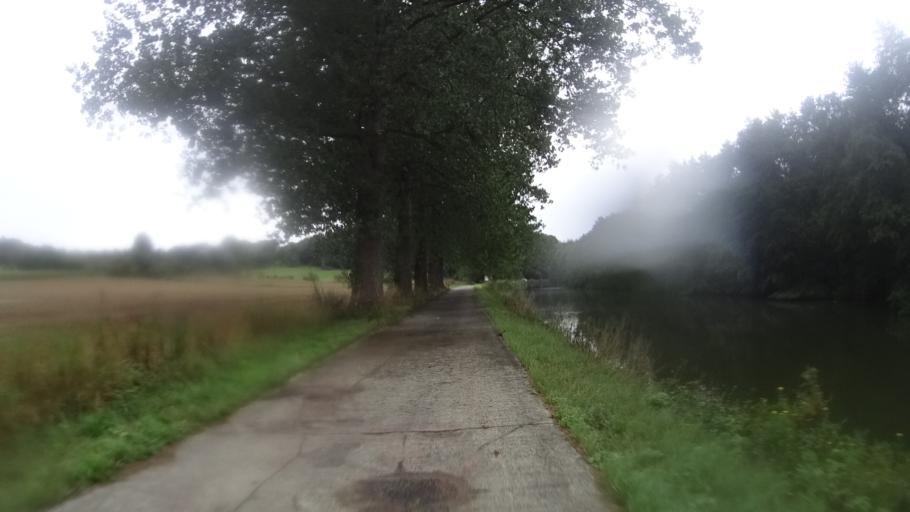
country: BE
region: Wallonia
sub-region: Province du Hainaut
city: Lobbes
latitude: 50.3449
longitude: 4.2487
